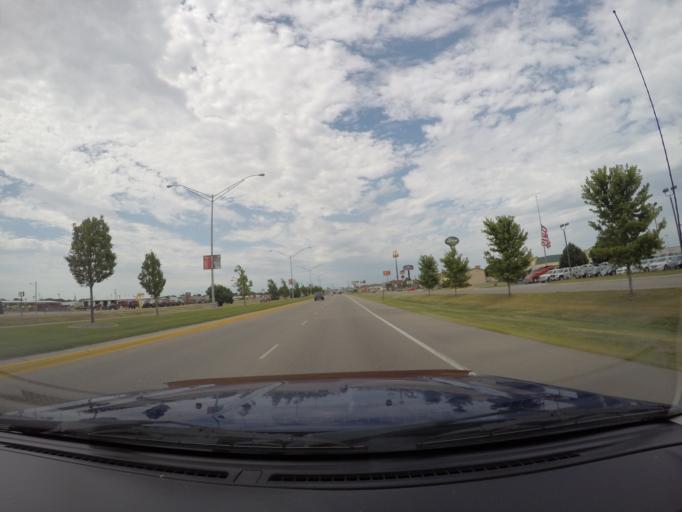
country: US
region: Nebraska
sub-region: Buffalo County
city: Kearney
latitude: 40.6791
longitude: -99.0848
